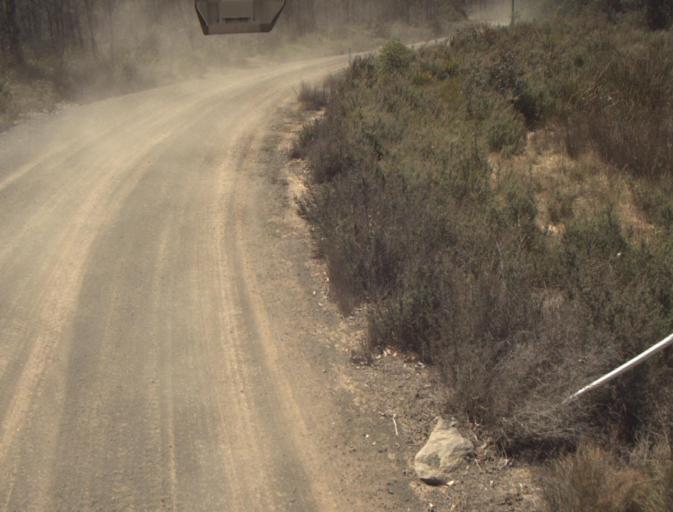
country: AU
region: Tasmania
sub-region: Launceston
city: Mayfield
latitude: -41.2795
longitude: 147.0958
